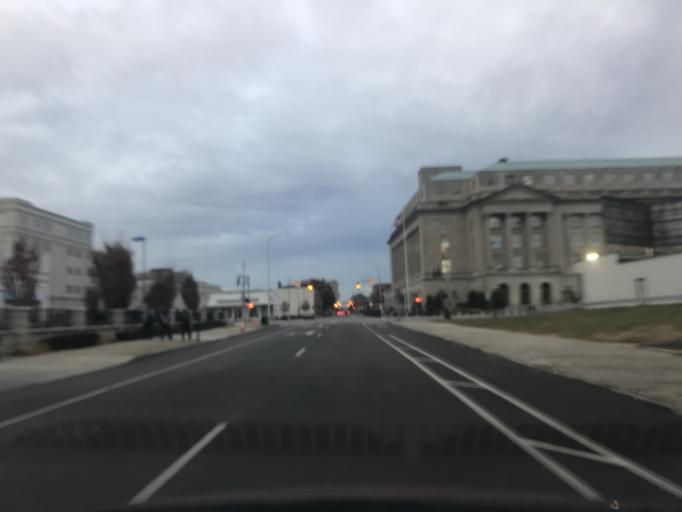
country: US
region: Kentucky
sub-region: Jefferson County
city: Louisville
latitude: 38.2458
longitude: -85.7635
